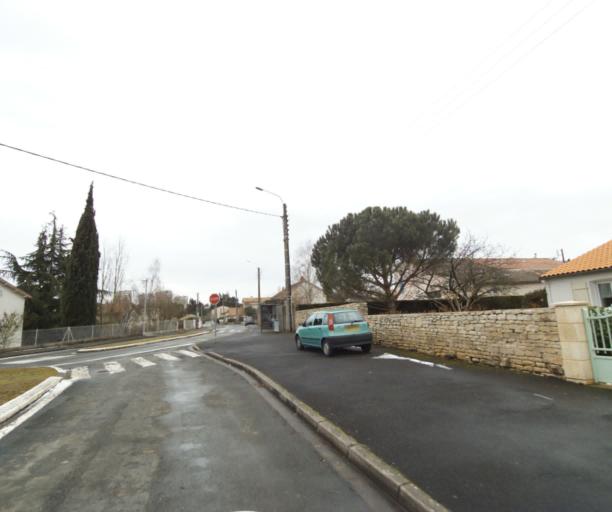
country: FR
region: Poitou-Charentes
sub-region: Departement des Deux-Sevres
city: Niort
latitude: 46.3392
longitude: -0.4558
